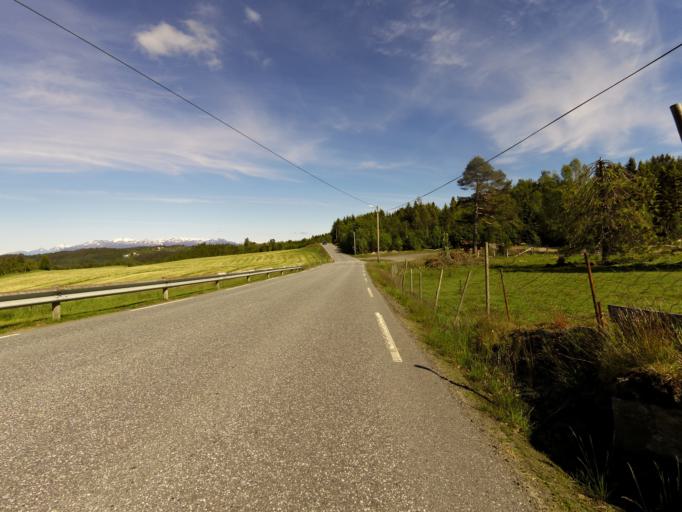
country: NO
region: Hordaland
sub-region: Stord
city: Leirvik
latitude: 59.7881
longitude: 5.4695
